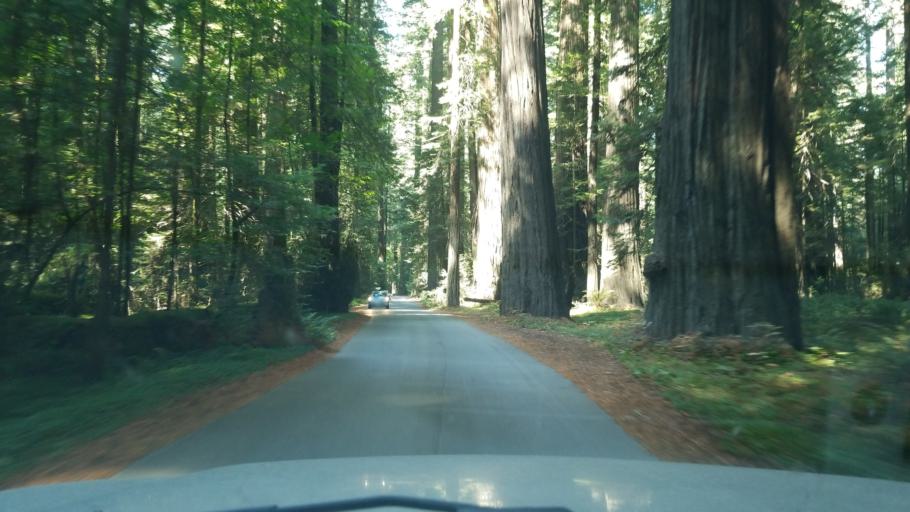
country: US
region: California
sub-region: Humboldt County
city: Rio Dell
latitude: 40.3498
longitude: -123.9195
